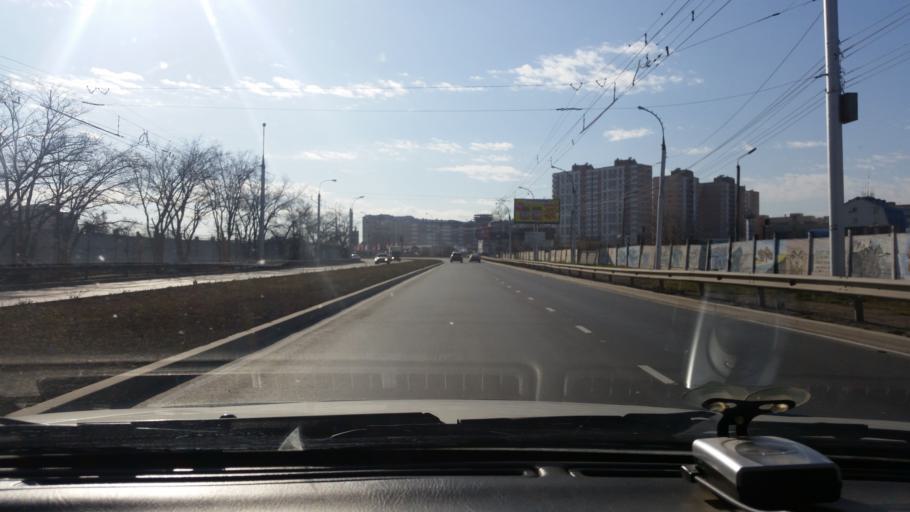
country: RU
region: Irkutsk
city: Dzerzhinsk
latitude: 52.2688
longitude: 104.3482
